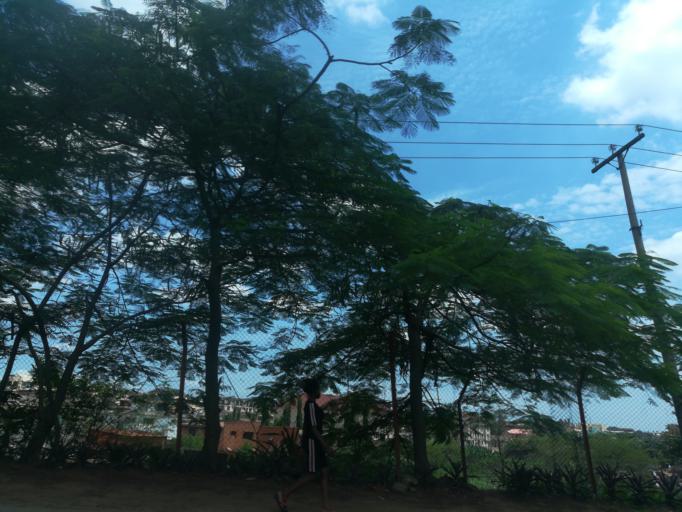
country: NG
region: Lagos
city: Ikeja
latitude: 6.6084
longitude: 3.3510
